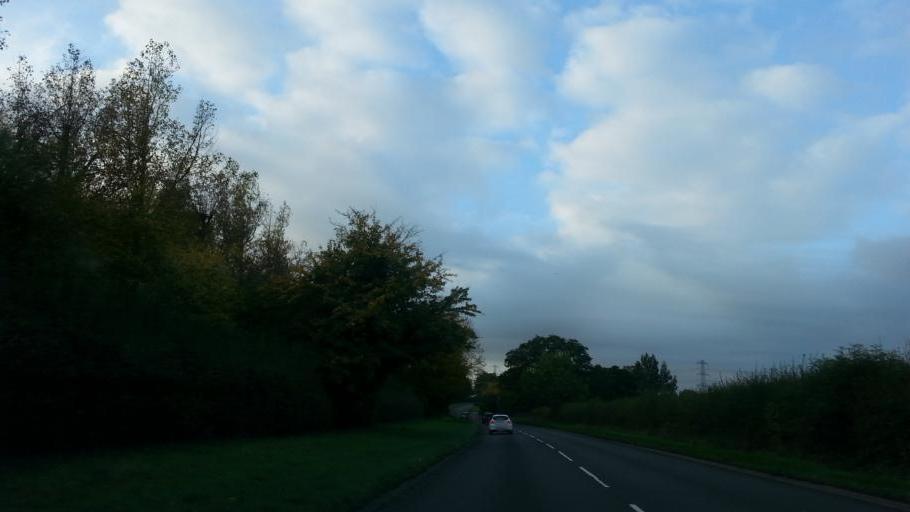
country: GB
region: England
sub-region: Staffordshire
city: Fazeley
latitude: 52.6108
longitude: -1.7456
